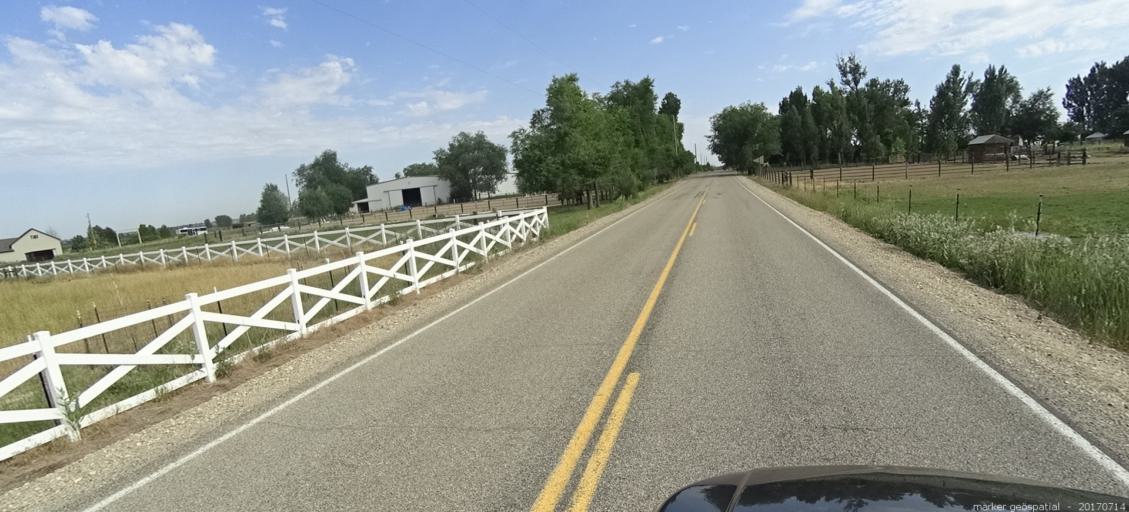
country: US
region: Idaho
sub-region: Ada County
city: Kuna
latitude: 43.4900
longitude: -116.3543
